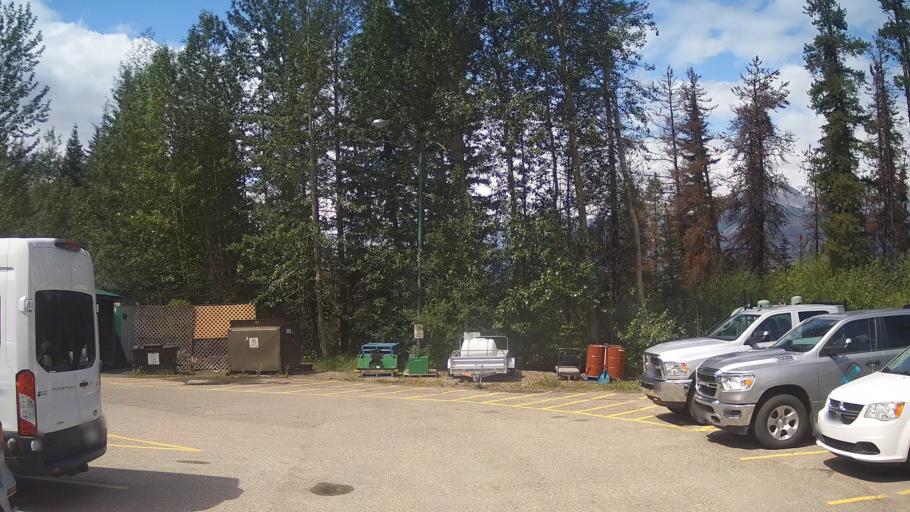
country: CA
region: Alberta
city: Jasper Park Lodge
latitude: 52.8507
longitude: -118.1243
